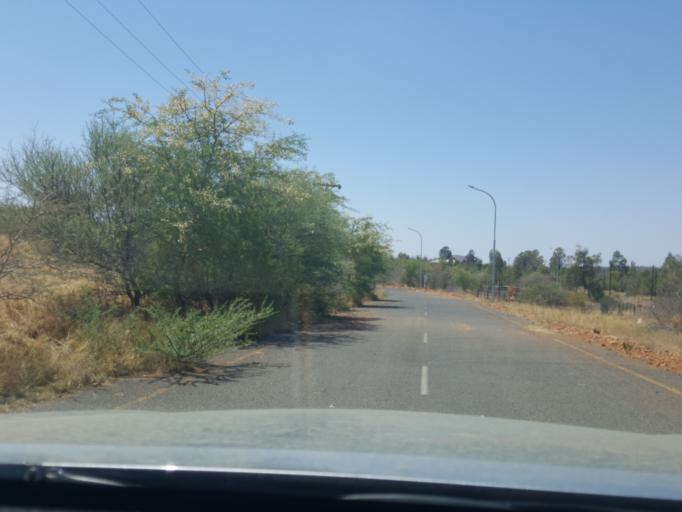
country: BW
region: South East
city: Lobatse
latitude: -25.1852
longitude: 25.6798
